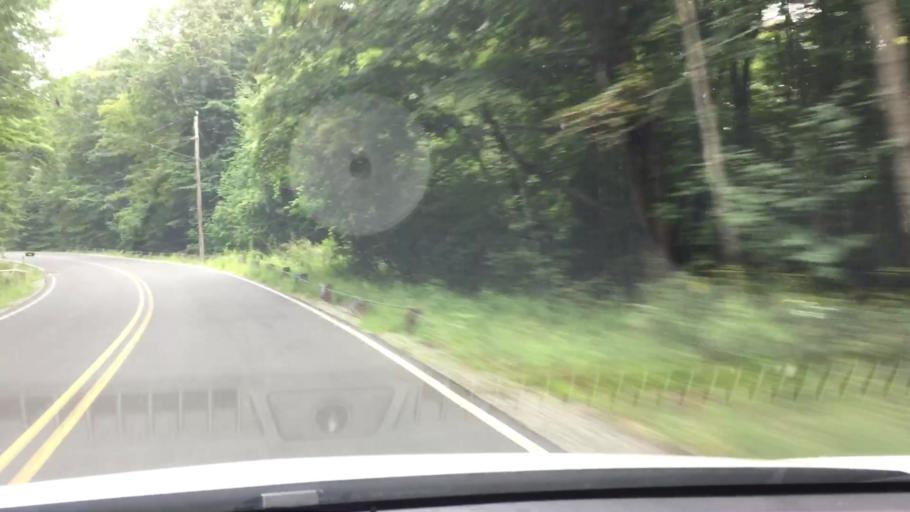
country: US
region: Massachusetts
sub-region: Berkshire County
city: Otis
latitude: 42.2302
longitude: -72.9760
